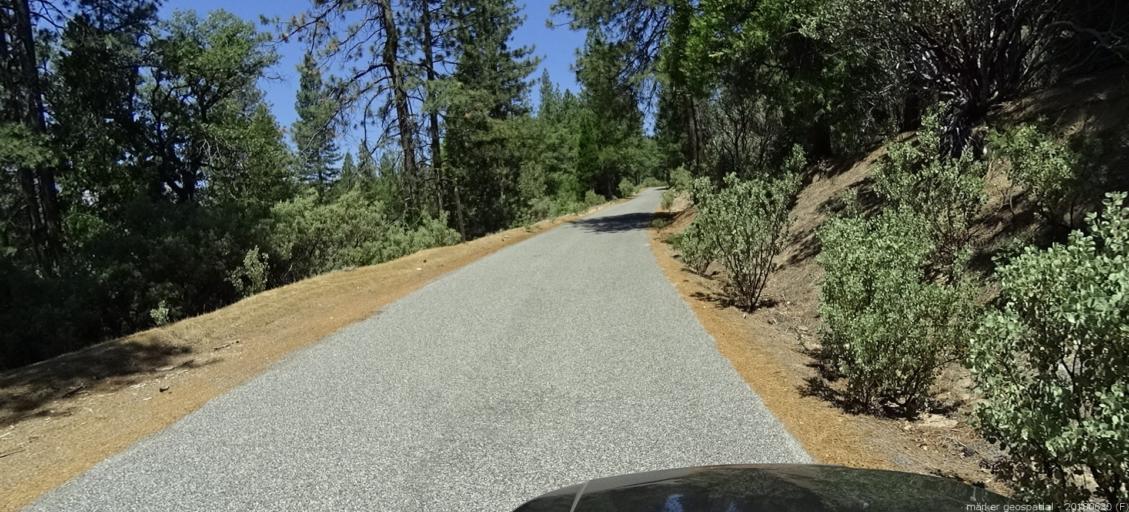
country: US
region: California
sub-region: Madera County
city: Oakhurst
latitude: 37.3811
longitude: -119.3603
